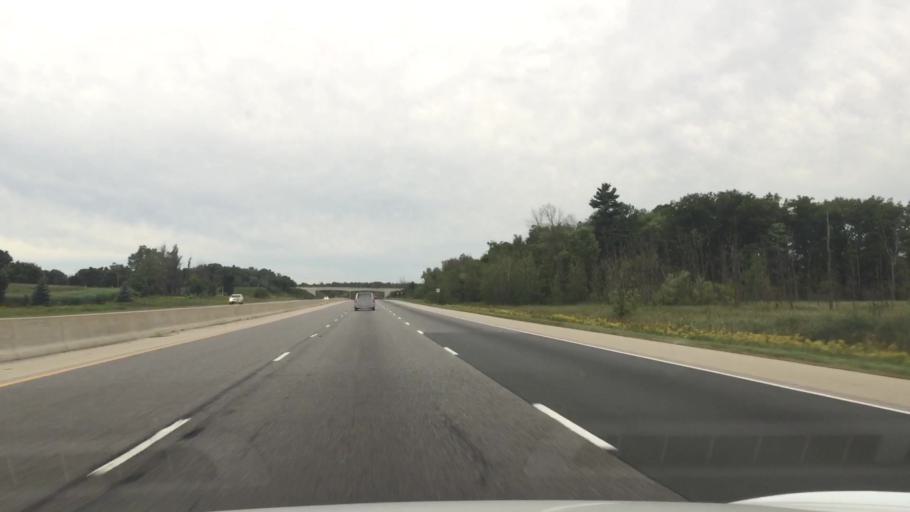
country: CA
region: Ontario
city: Kitchener
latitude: 43.2638
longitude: -80.5580
